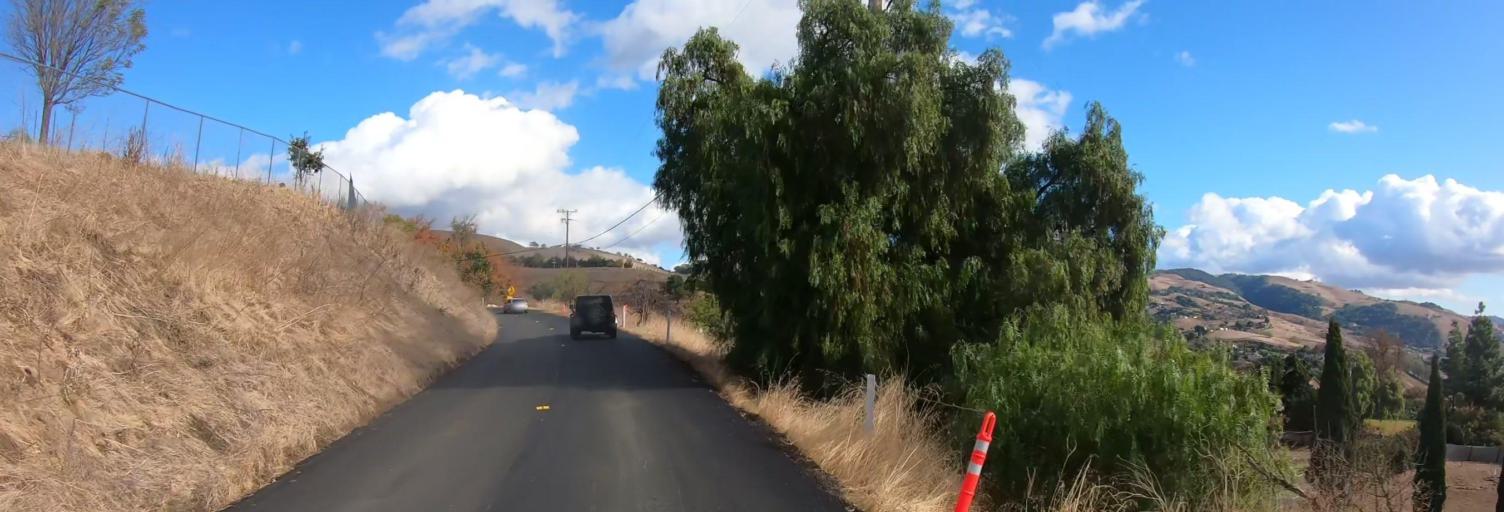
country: US
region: California
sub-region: Santa Clara County
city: East Foothills
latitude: 37.3759
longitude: -121.7930
